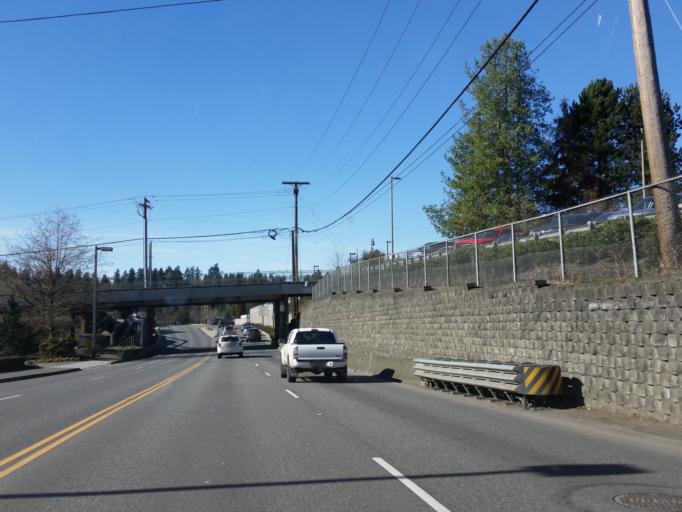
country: US
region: Washington
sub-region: King County
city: Bothell
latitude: 47.7594
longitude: -122.2027
